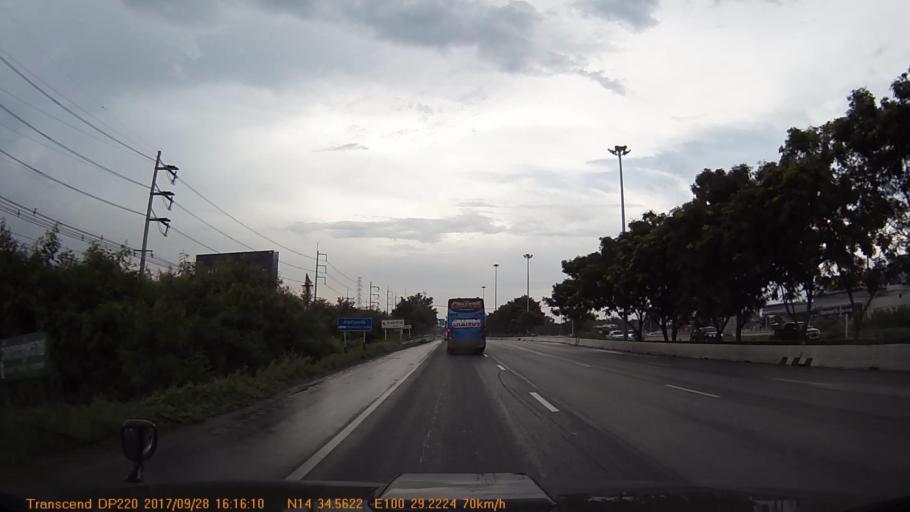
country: TH
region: Ang Thong
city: Ang Thong
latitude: 14.5767
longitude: 100.4866
